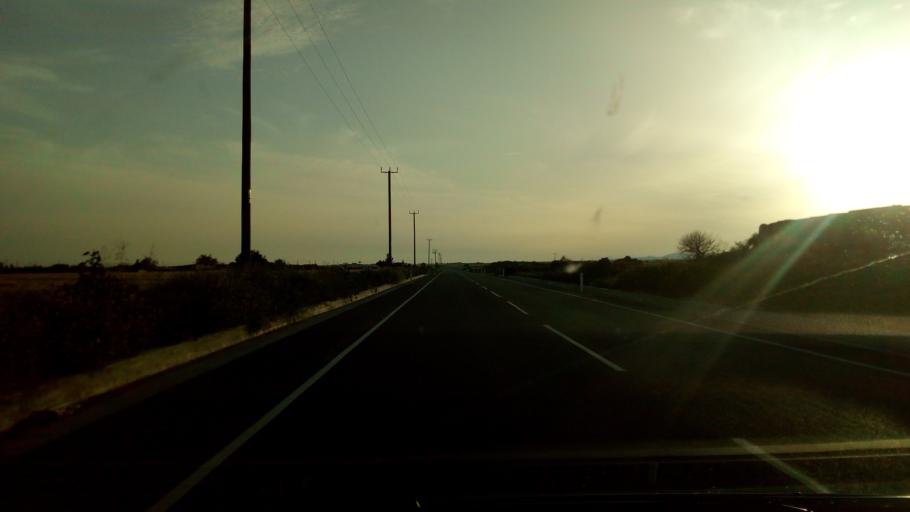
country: CY
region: Larnaka
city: Tersefanou
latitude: 34.8358
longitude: 33.5511
